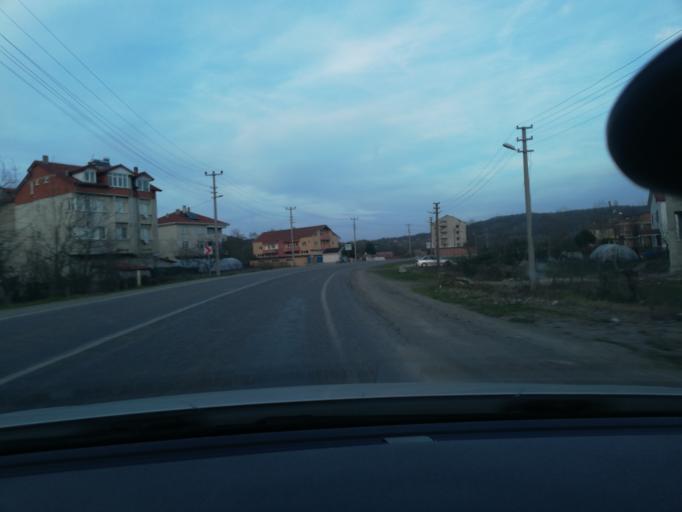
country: TR
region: Zonguldak
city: Saltukova
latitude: 41.5267
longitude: 32.0963
